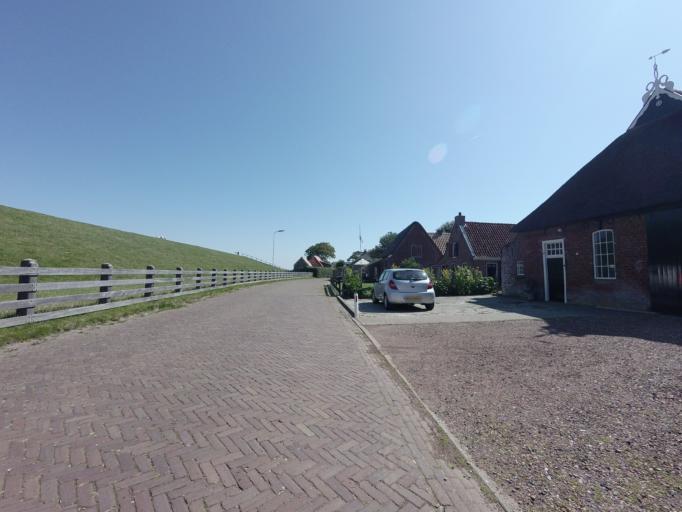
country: NL
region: Friesland
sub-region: Gemeente Dongeradeel
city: Anjum
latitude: 53.4025
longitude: 6.0852
